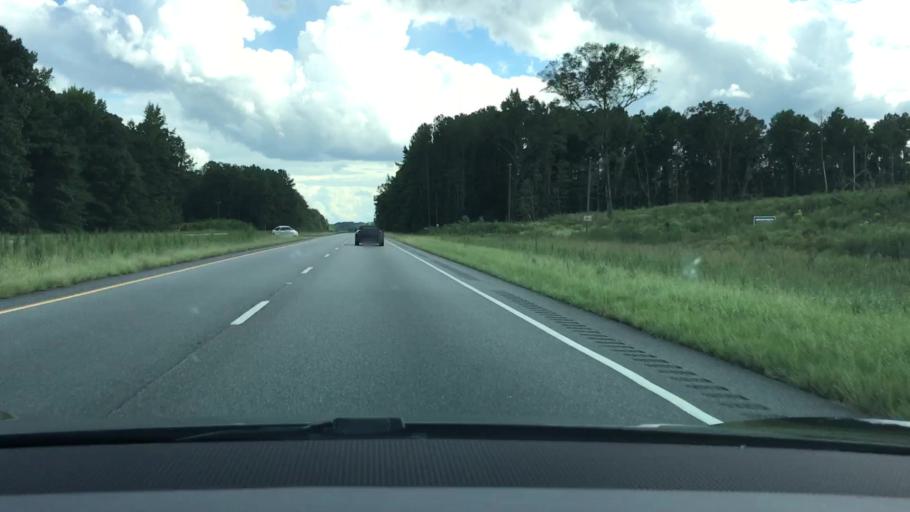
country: US
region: Alabama
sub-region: Pike County
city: Troy
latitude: 31.9422
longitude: -86.0226
